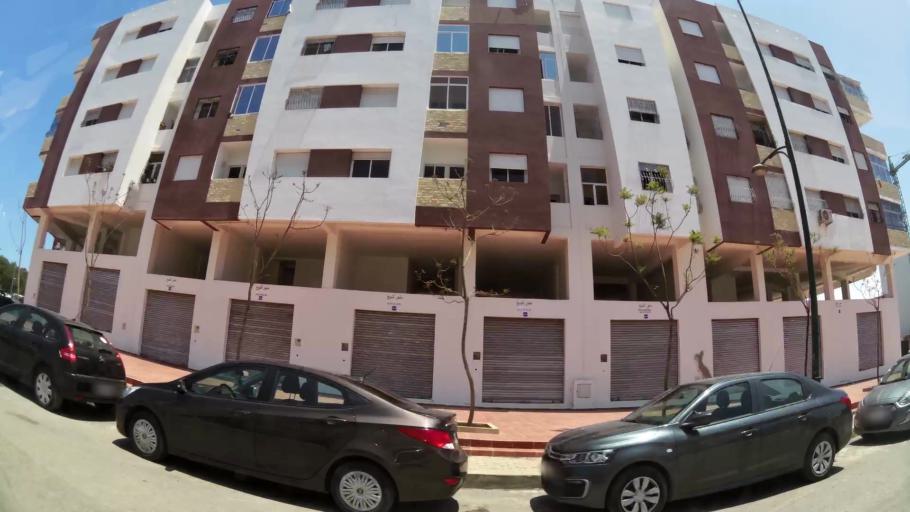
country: MA
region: Gharb-Chrarda-Beni Hssen
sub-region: Kenitra Province
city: Kenitra
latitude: 34.2710
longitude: -6.6280
